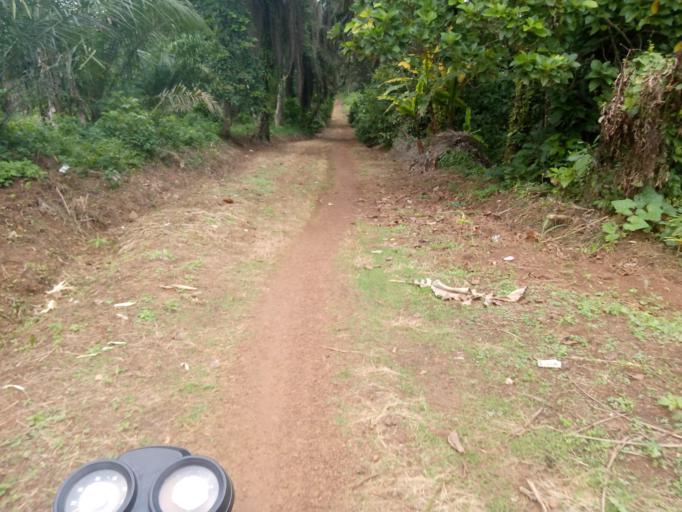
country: SL
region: Eastern Province
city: Buedu
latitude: 8.4806
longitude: -10.3281
